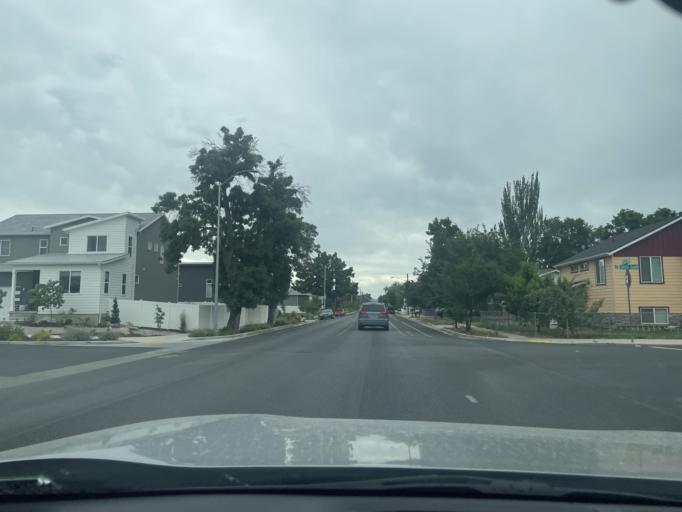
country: US
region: Utah
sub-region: Salt Lake County
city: Millcreek
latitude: 40.6980
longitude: -111.8770
